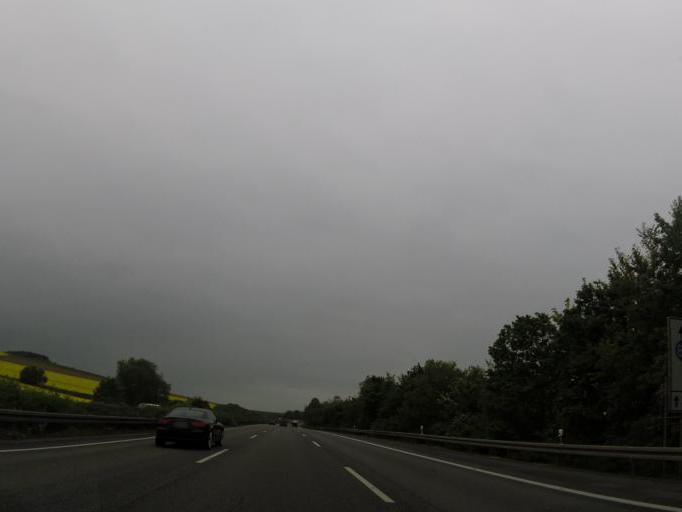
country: DE
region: Lower Saxony
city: Kalefeld
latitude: 51.7764
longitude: 10.0297
